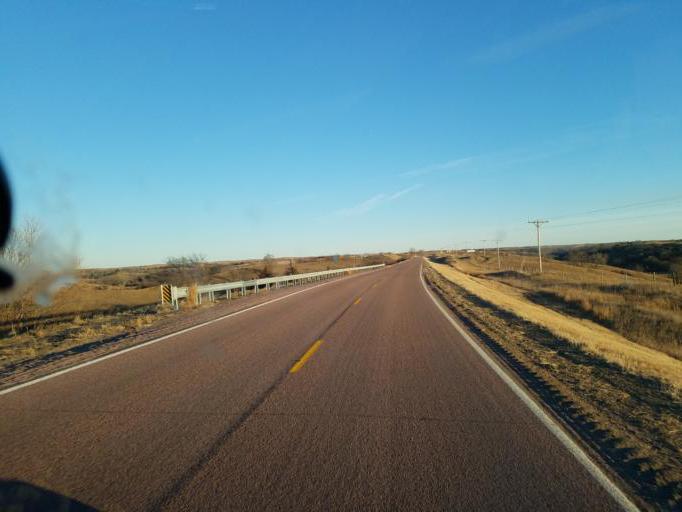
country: US
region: South Dakota
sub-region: Bon Homme County
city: Springfield
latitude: 42.7410
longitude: -97.9153
